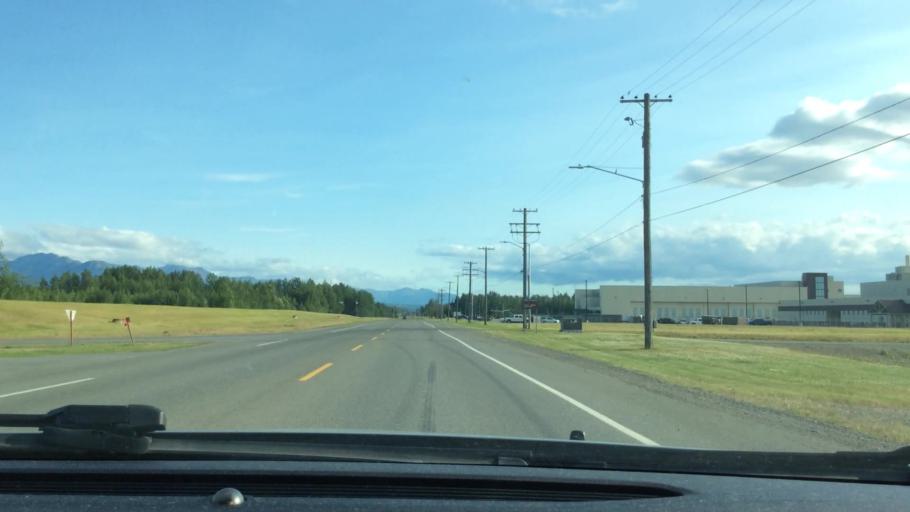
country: US
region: Alaska
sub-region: Anchorage Municipality
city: Anchorage
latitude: 61.2466
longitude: -149.7786
